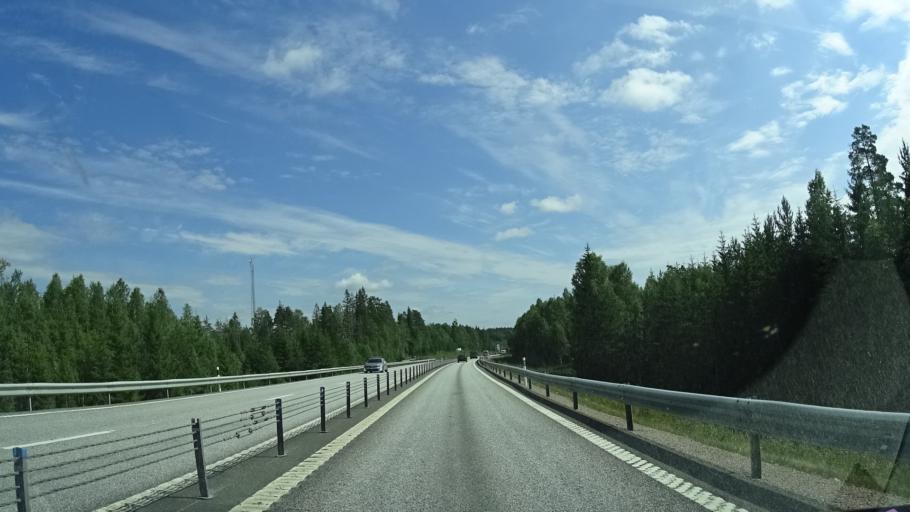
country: SE
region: OErebro
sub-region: Degerfors Kommun
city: Degerfors
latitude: 59.3231
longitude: 14.3593
